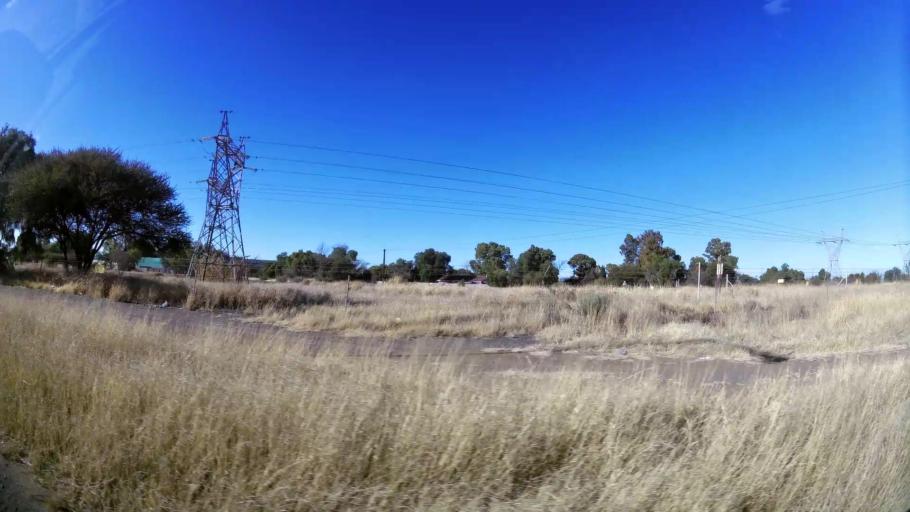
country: ZA
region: Northern Cape
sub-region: Frances Baard District Municipality
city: Kimberley
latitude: -28.7476
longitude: 24.7955
